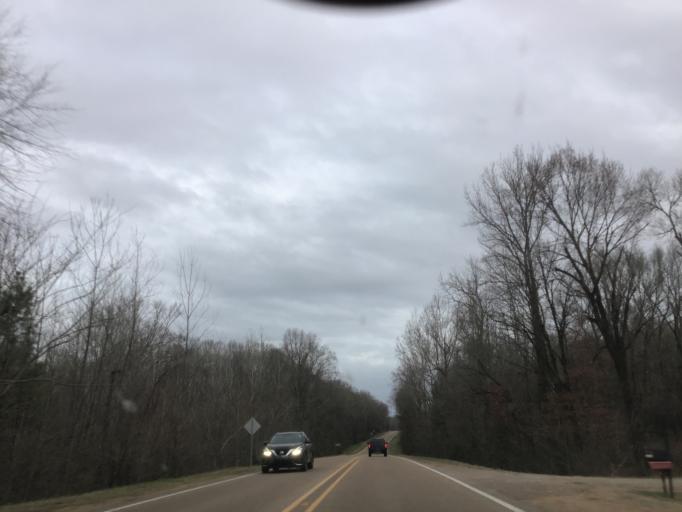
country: US
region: Mississippi
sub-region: Warren County
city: Beechwood
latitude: 32.3176
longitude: -90.8122
